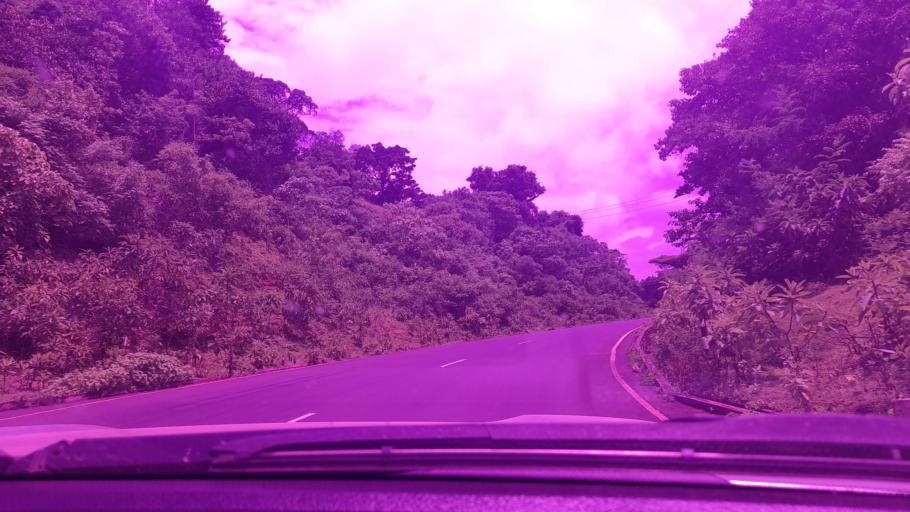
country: ET
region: Oromiya
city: Metu
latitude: 8.3387
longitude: 35.7434
